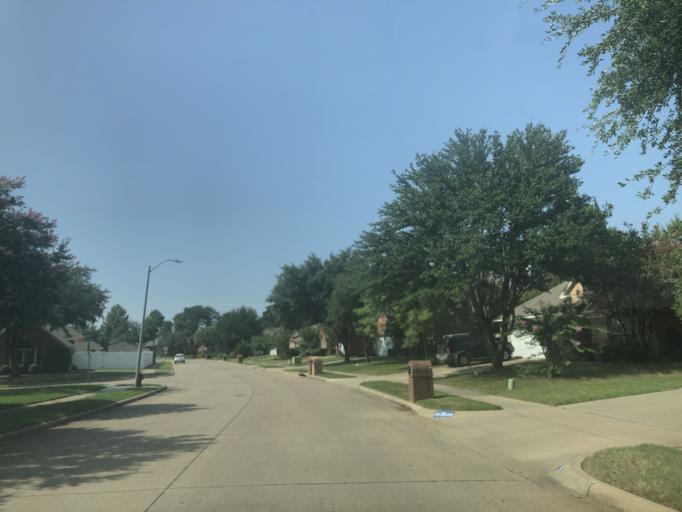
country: US
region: Texas
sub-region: Dallas County
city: Grand Prairie
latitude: 32.7710
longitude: -97.0409
